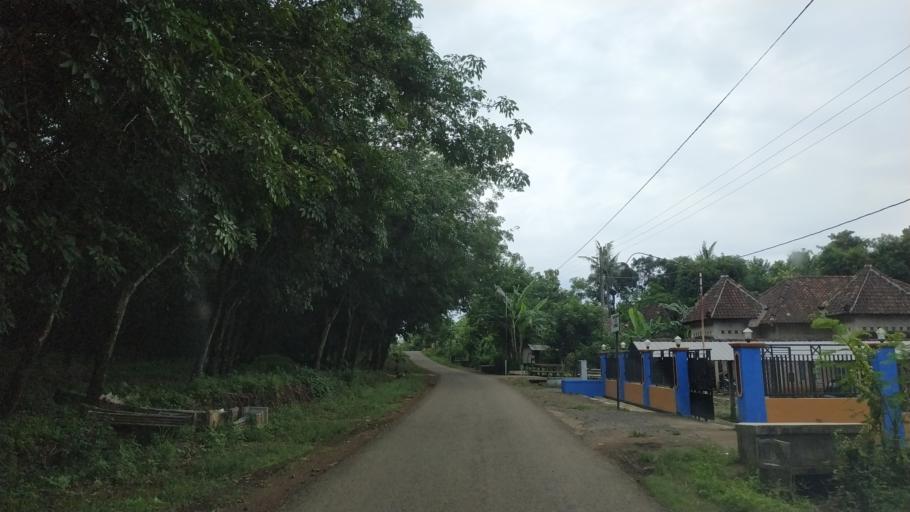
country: ID
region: Central Java
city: Krajan Tegalombo
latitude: -6.4322
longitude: 110.9830
